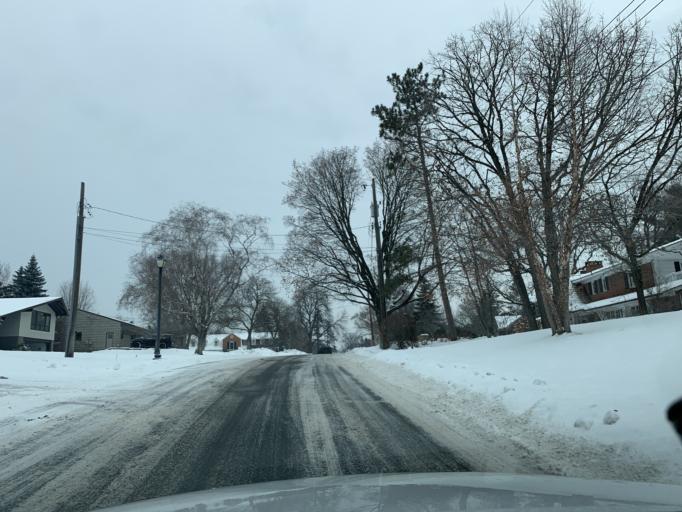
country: US
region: Minnesota
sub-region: Hennepin County
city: Edina
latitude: 44.9140
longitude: -93.3461
